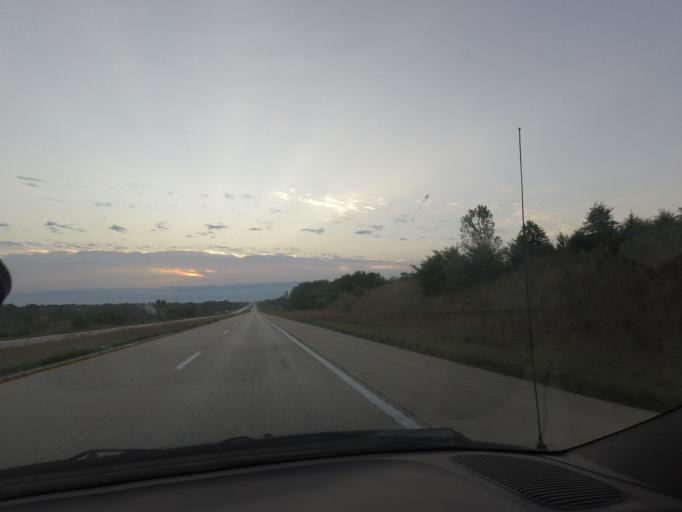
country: US
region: Missouri
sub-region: Macon County
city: Macon
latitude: 39.7543
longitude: -92.4254
